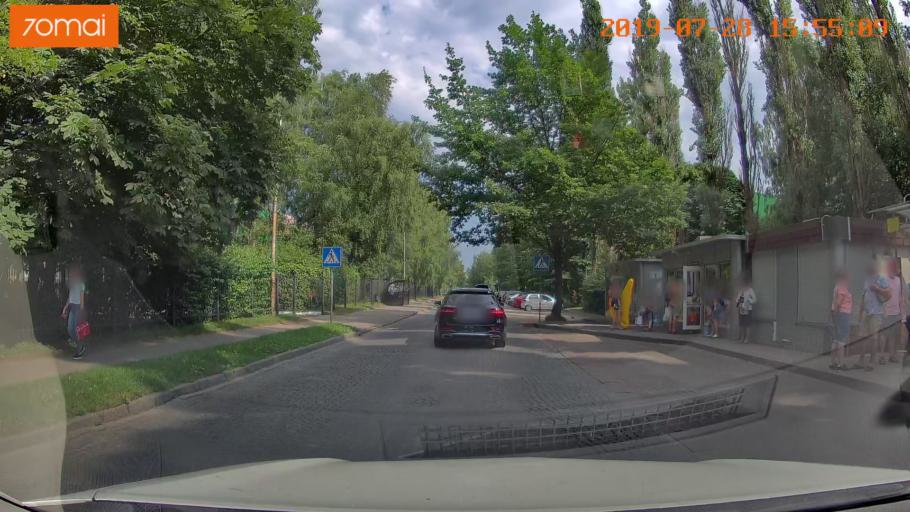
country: RU
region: Kaliningrad
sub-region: Gorod Svetlogorsk
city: Svetlogorsk
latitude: 54.9413
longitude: 20.1383
